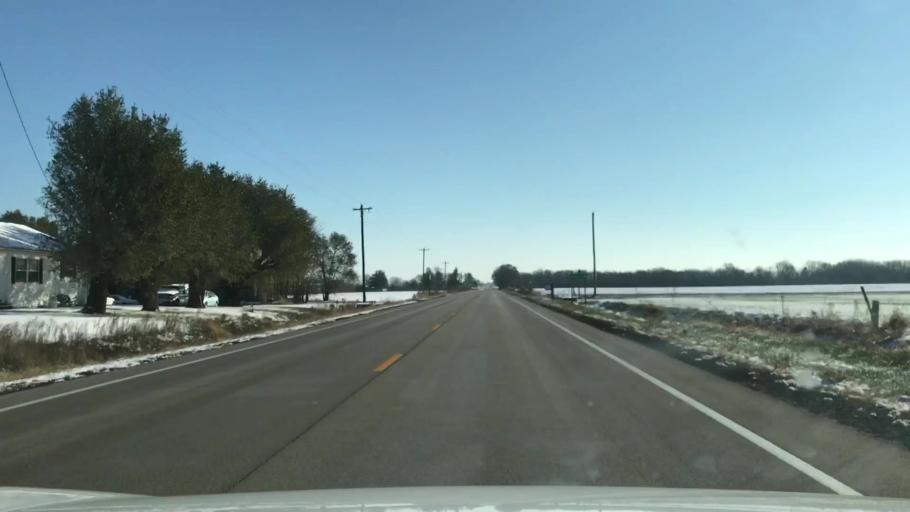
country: US
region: Illinois
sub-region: Washington County
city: Okawville
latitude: 38.4419
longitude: -89.4791
